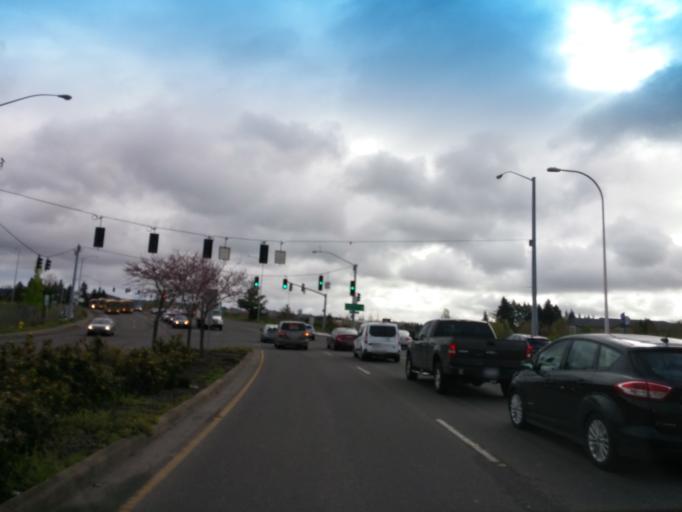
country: US
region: Oregon
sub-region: Washington County
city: Oak Hills
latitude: 45.5294
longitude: -122.8410
